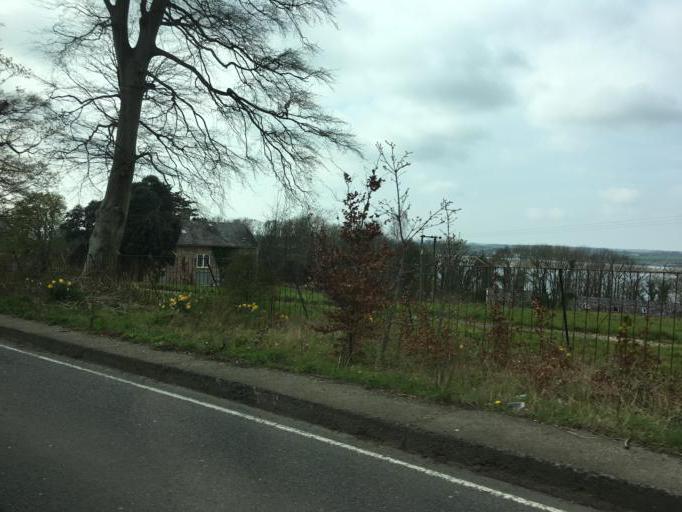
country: GB
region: Wales
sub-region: Gwynedd
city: Caernarfon
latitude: 53.1564
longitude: -4.2568
